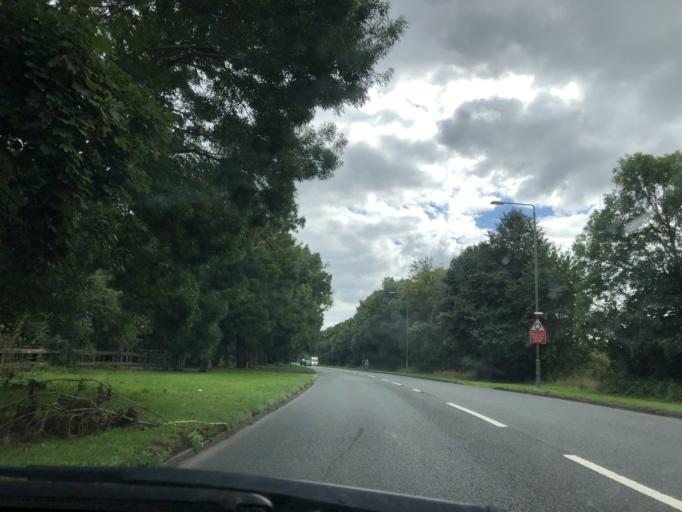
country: GB
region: England
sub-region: Kent
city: Halstead
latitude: 51.3495
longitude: 0.1312
